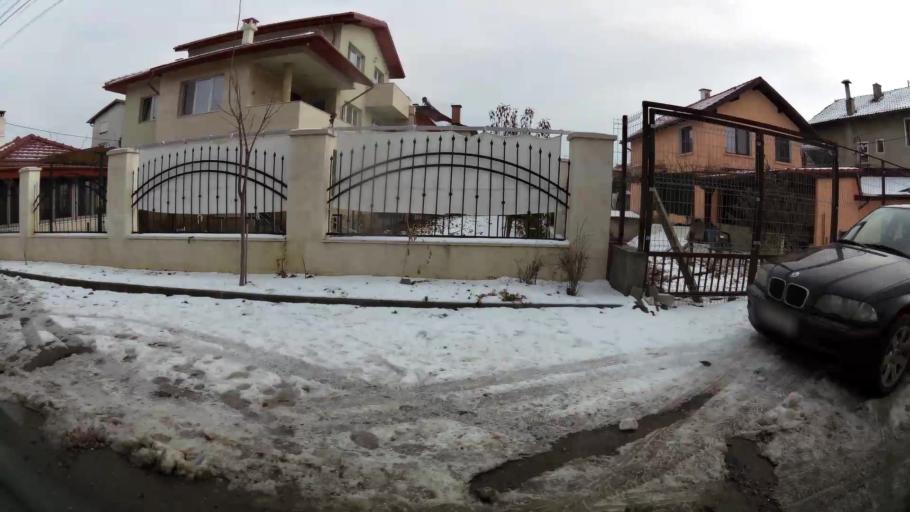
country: BG
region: Sofia-Capital
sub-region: Stolichna Obshtina
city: Sofia
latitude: 42.7149
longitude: 23.4147
